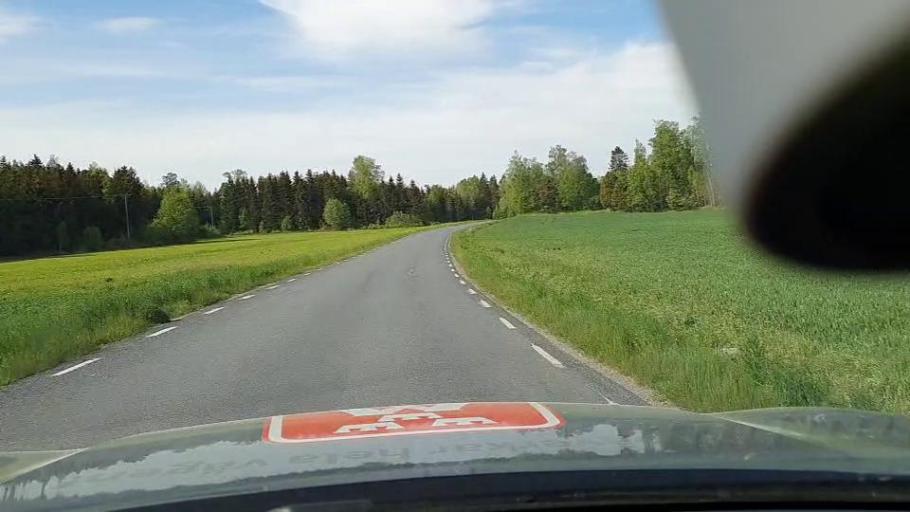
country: SE
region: Soedermanland
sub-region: Eskilstuna Kommun
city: Arla
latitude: 59.2740
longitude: 16.6669
